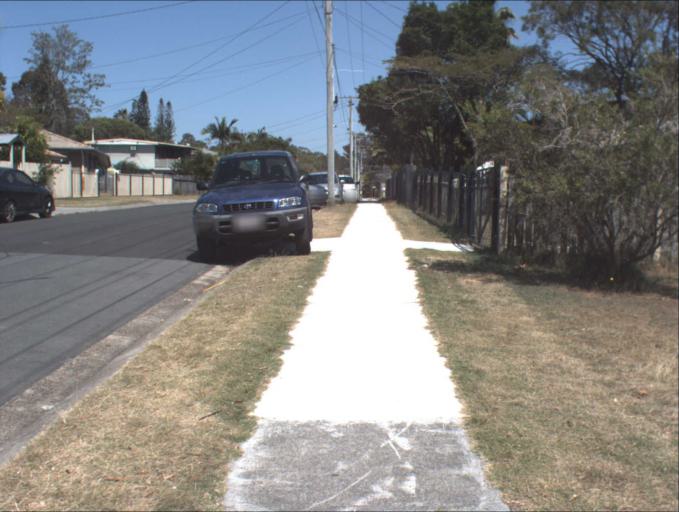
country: AU
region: Queensland
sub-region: Logan
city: Beenleigh
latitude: -27.7027
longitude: 153.2082
